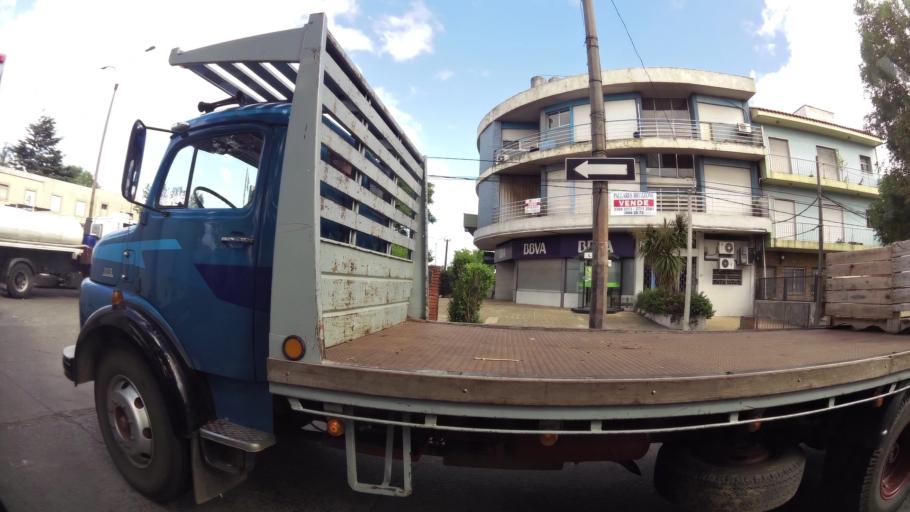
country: UY
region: Montevideo
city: Montevideo
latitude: -34.8721
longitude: -56.1569
